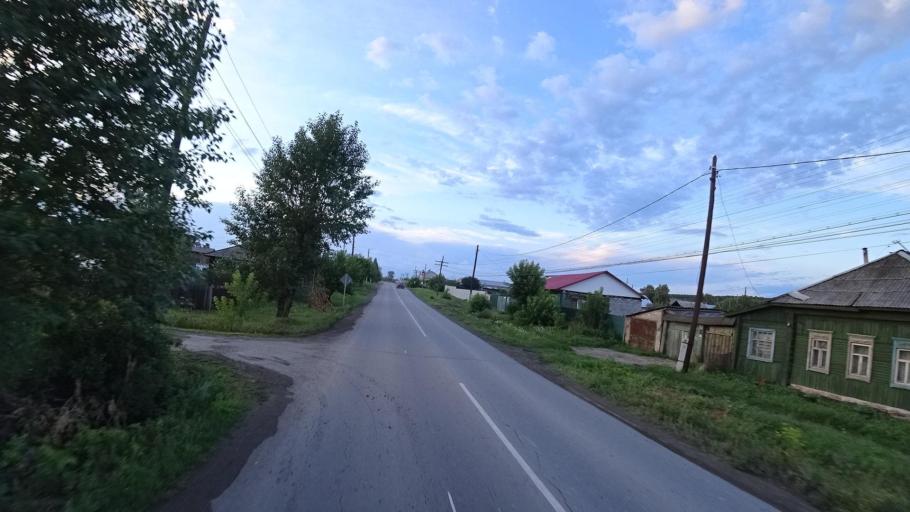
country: RU
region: Sverdlovsk
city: Kamyshlov
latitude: 56.8620
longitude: 62.7088
